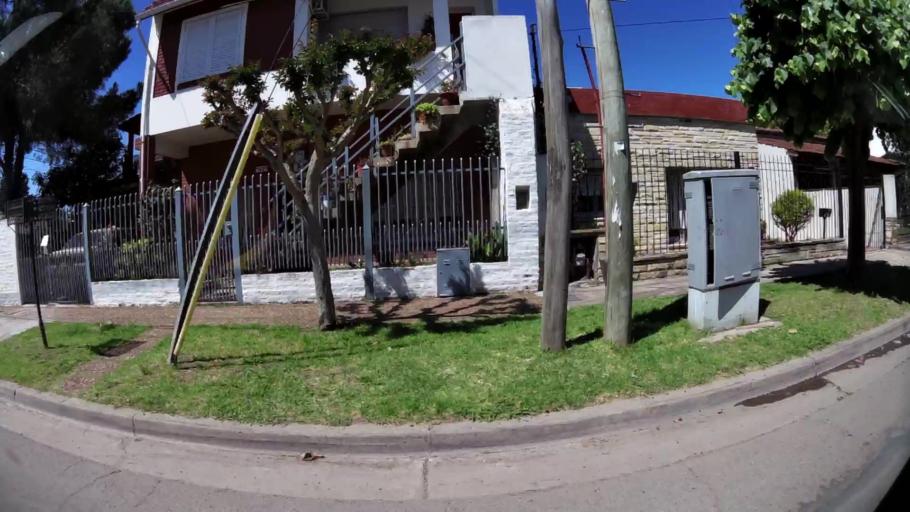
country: AR
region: Buenos Aires
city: Ituzaingo
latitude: -34.6633
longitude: -58.6537
